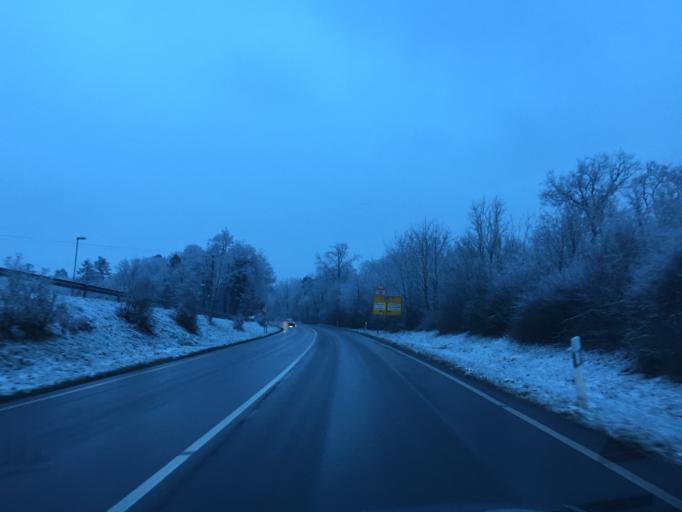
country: DE
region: Baden-Wuerttemberg
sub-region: Karlsruhe Region
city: Oftersheim
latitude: 49.3593
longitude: 8.5862
